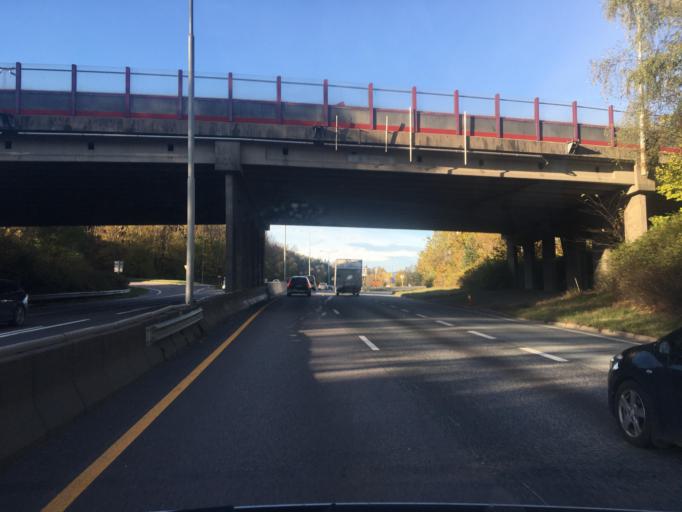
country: NO
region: Oslo
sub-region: Oslo
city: Oslo
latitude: 59.8876
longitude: 10.8079
